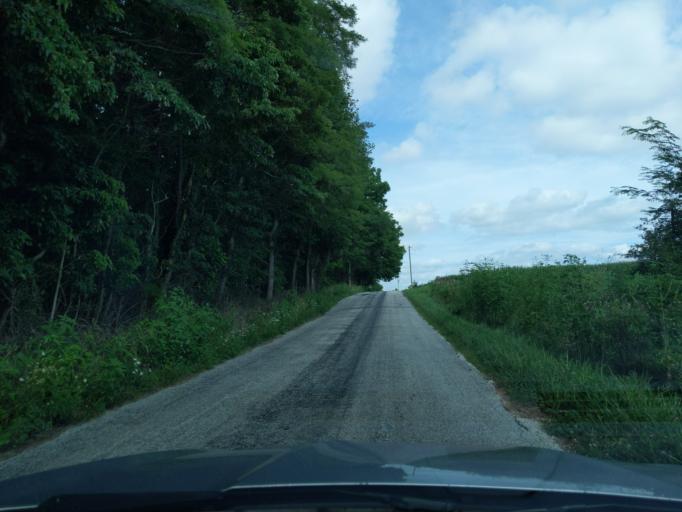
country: US
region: Indiana
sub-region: Decatur County
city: Greensburg
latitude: 39.2350
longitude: -85.3937
